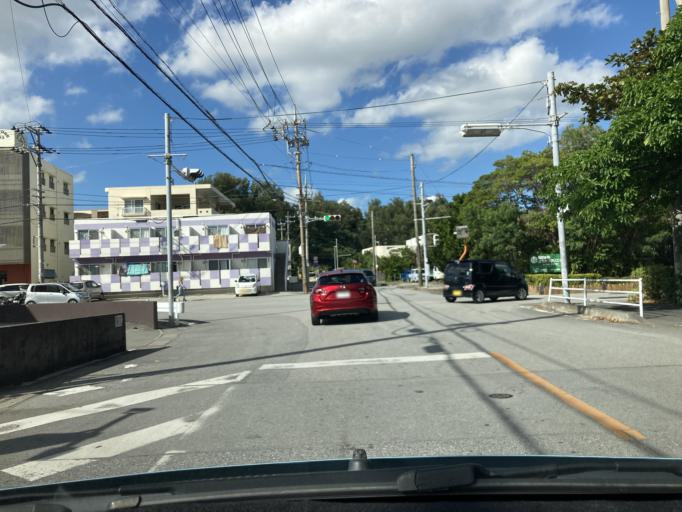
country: JP
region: Okinawa
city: Katsuren-haebaru
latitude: 26.3380
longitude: 127.8433
